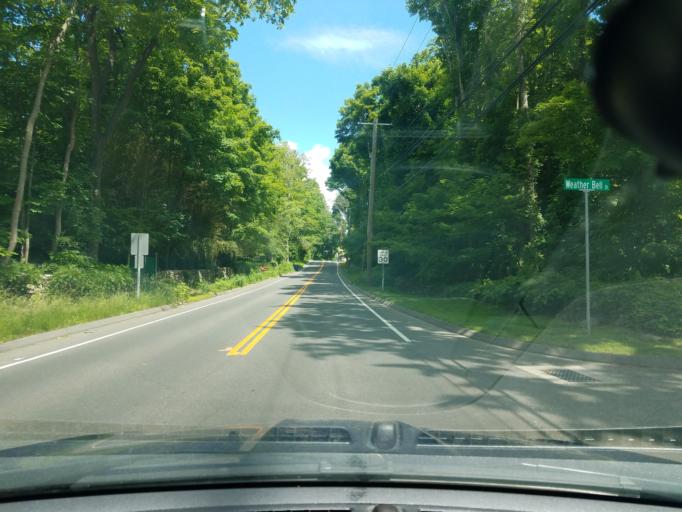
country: US
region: Connecticut
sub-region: Fairfield County
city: Westport
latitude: 41.1651
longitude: -73.3937
